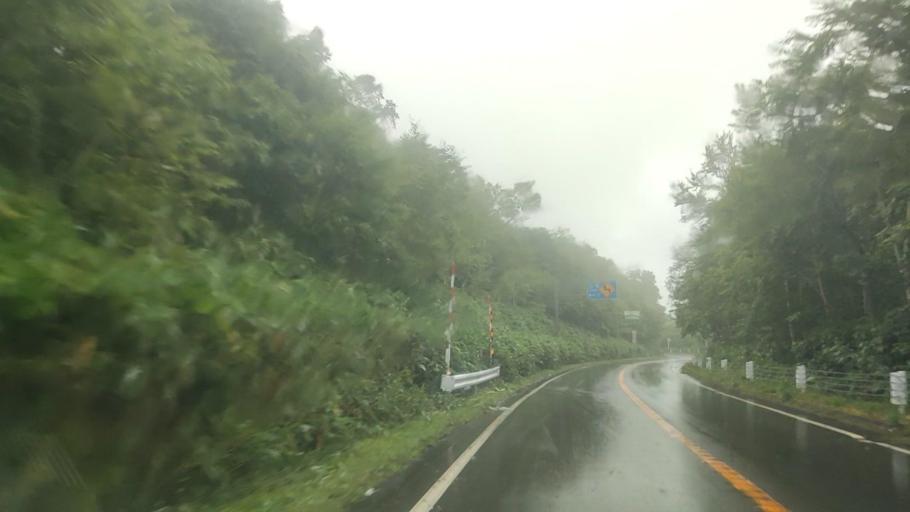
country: JP
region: Hokkaido
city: Shiraoi
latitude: 42.5459
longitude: 141.1033
